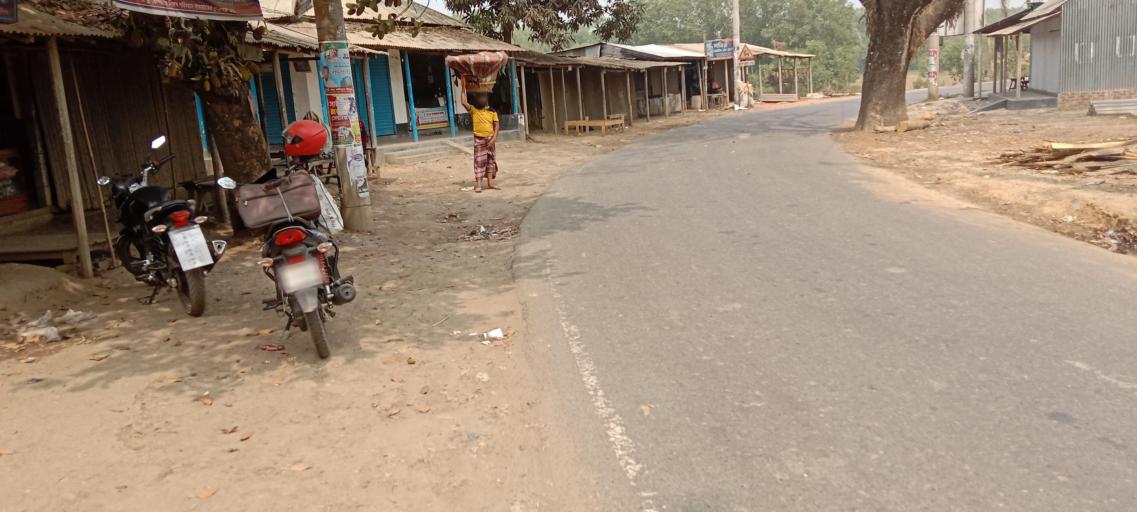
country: BD
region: Dhaka
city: Sakhipur
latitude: 24.4467
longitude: 90.3292
